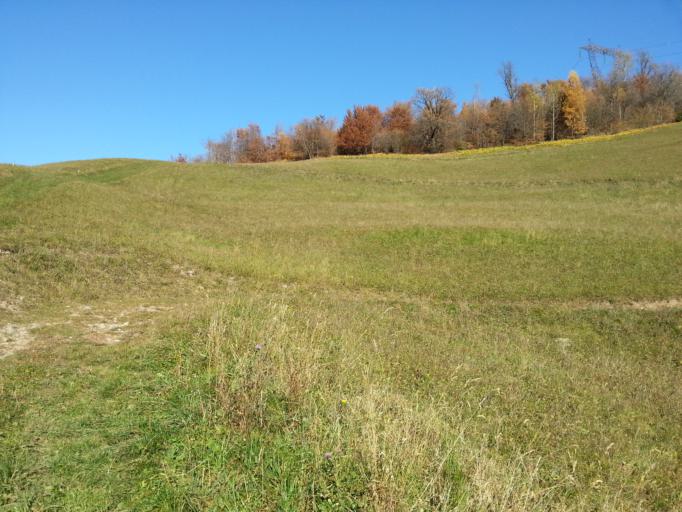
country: IT
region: Lombardy
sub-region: Provincia di Lecco
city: Primaluna
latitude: 45.9684
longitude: 9.4270
